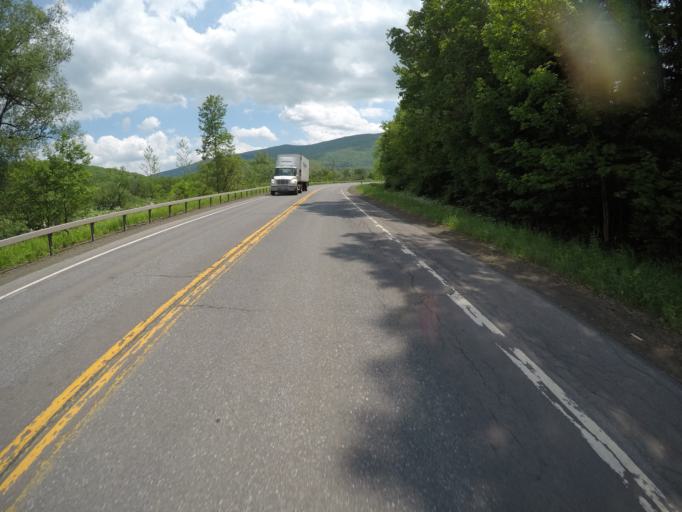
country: US
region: New York
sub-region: Delaware County
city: Stamford
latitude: 42.1566
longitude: -74.6243
